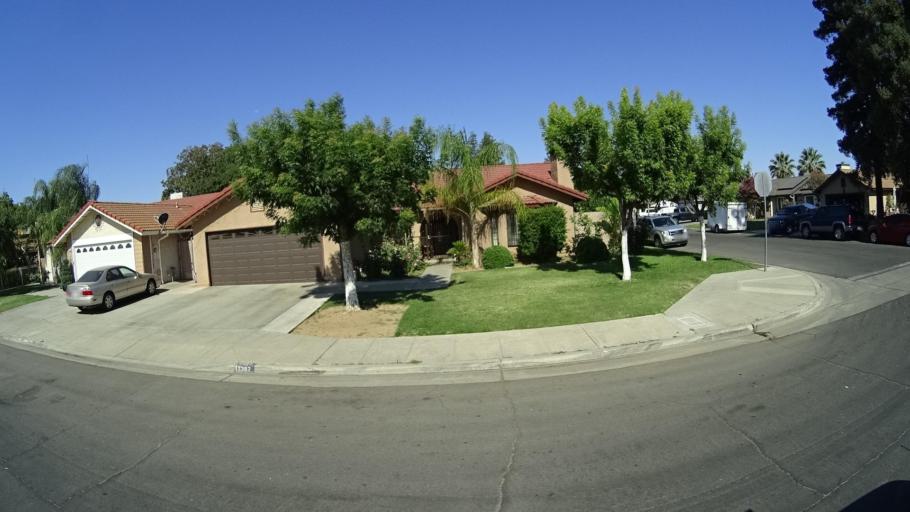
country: US
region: California
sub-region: Fresno County
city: Sunnyside
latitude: 36.7160
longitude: -119.7229
